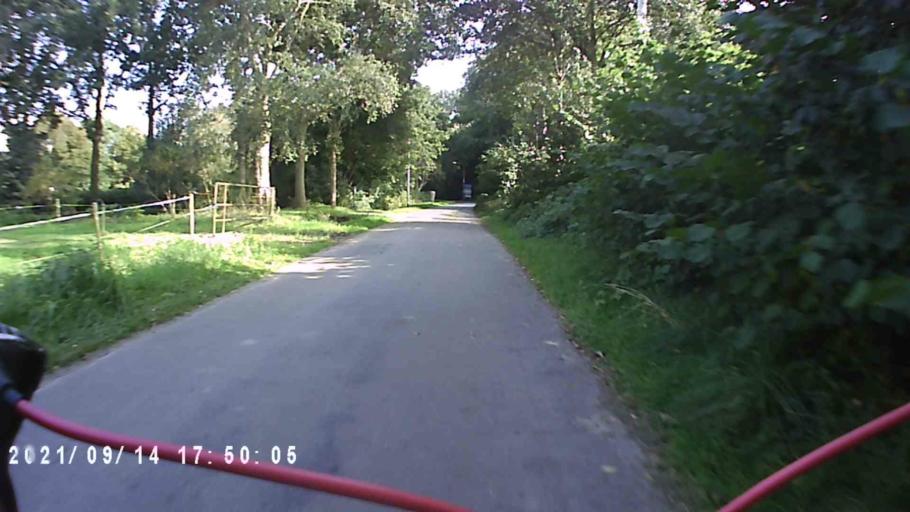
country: NL
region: Groningen
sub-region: Gemeente Haren
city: Haren
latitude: 53.1378
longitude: 6.6229
